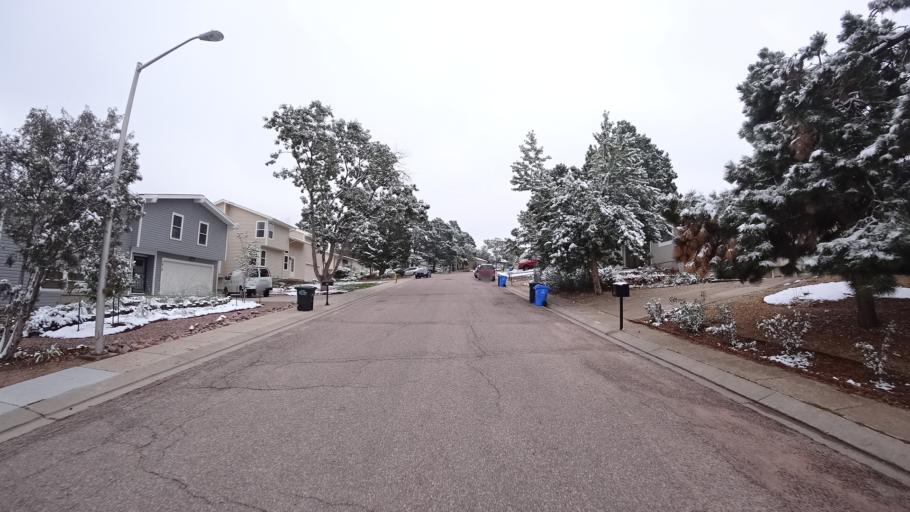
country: US
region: Colorado
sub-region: El Paso County
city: Cimarron Hills
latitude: 38.9229
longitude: -104.7707
